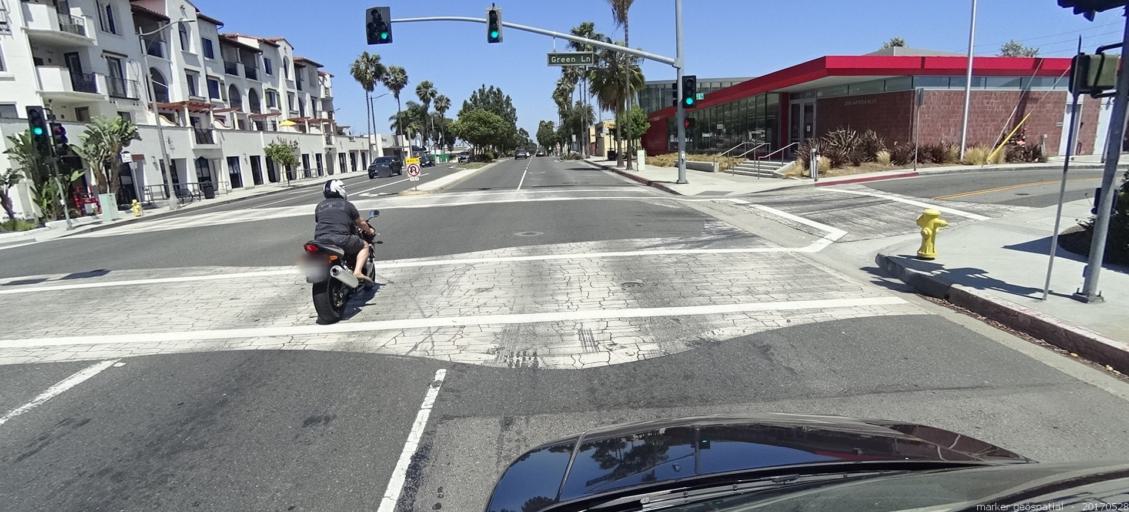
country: US
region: California
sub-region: Los Angeles County
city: Hermosa Beach
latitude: 33.8728
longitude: -118.3772
